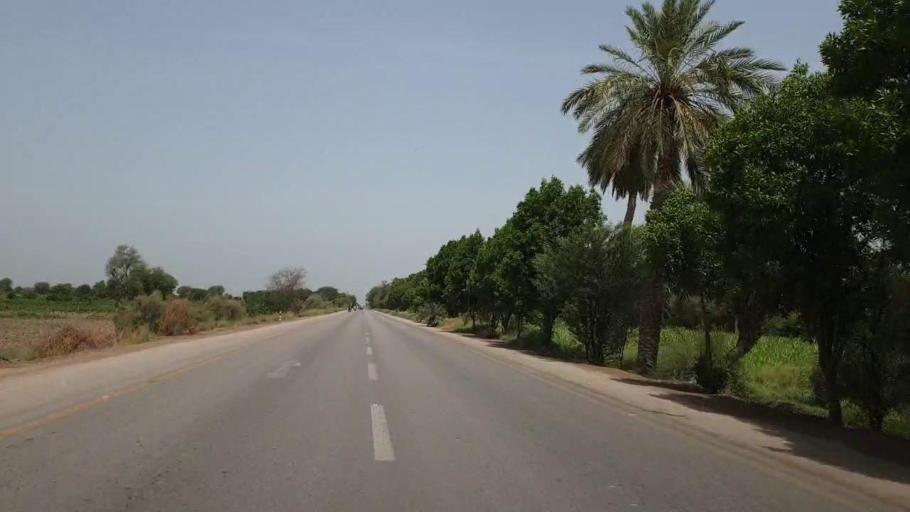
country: PK
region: Sindh
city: Nawabshah
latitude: 26.2189
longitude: 68.5025
